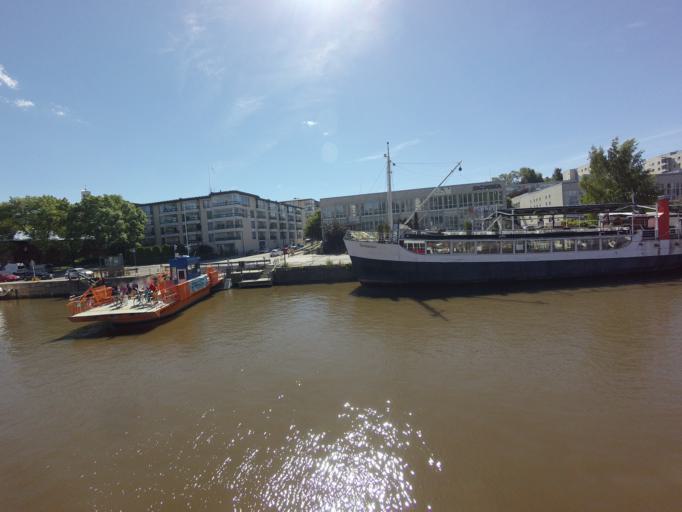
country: FI
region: Varsinais-Suomi
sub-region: Turku
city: Turku
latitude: 60.4410
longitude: 22.2479
